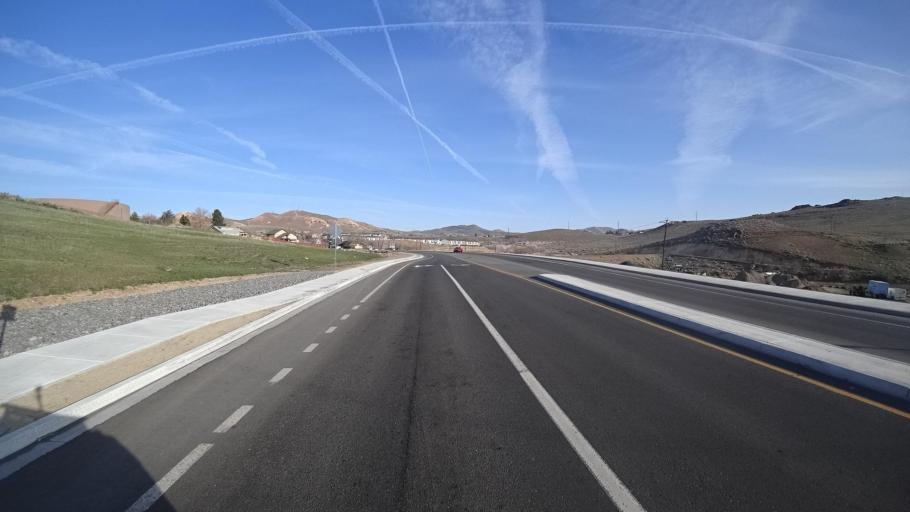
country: US
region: Nevada
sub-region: Washoe County
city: Sun Valley
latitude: 39.5649
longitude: -119.7739
